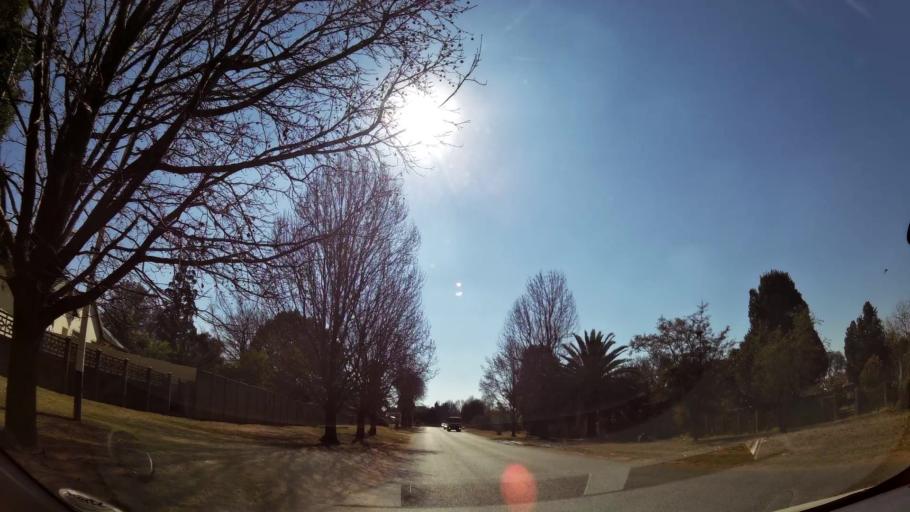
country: ZA
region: Mpumalanga
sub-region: Nkangala District Municipality
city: Witbank
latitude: -25.8309
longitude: 29.2433
